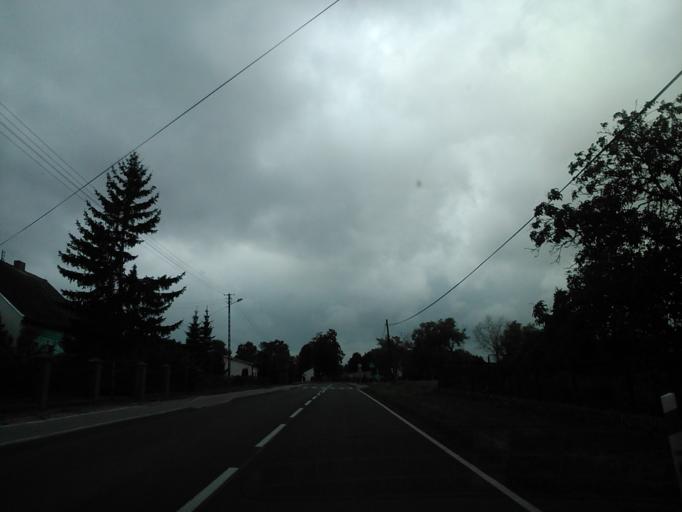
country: PL
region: Kujawsko-Pomorskie
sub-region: Powiat inowroclawski
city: Kruszwica
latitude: 52.6830
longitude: 18.2690
